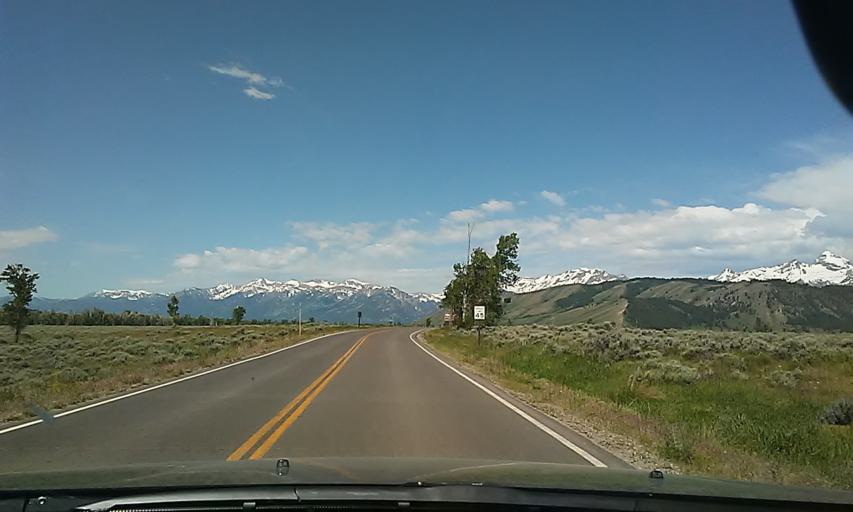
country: US
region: Wyoming
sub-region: Teton County
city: Jackson
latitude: 43.6252
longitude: -110.6299
